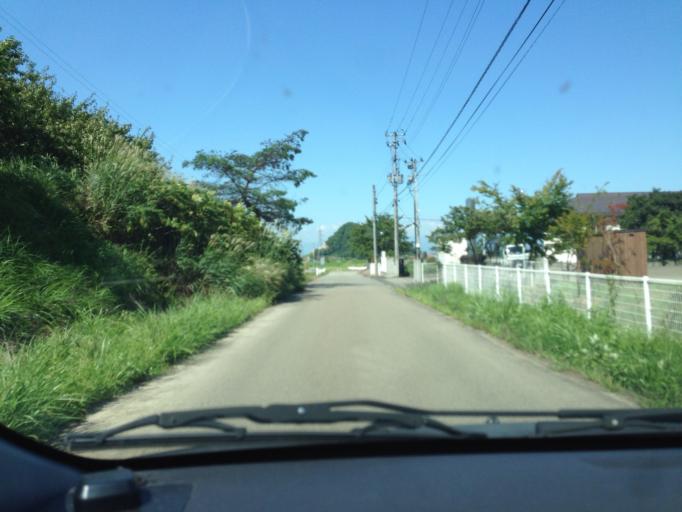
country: JP
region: Fukushima
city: Kitakata
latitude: 37.4349
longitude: 139.8786
